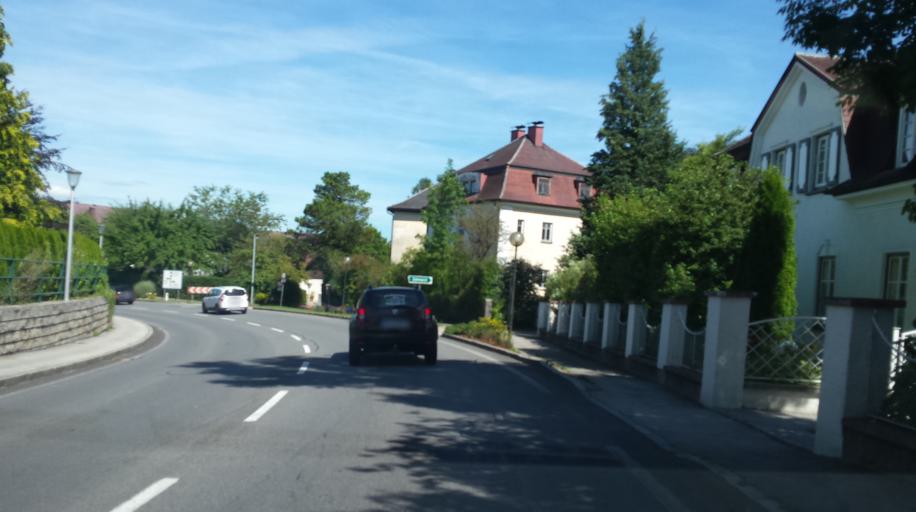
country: AT
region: Upper Austria
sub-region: Politischer Bezirk Vocklabruck
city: Frankenmarkt
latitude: 47.9844
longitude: 13.4153
